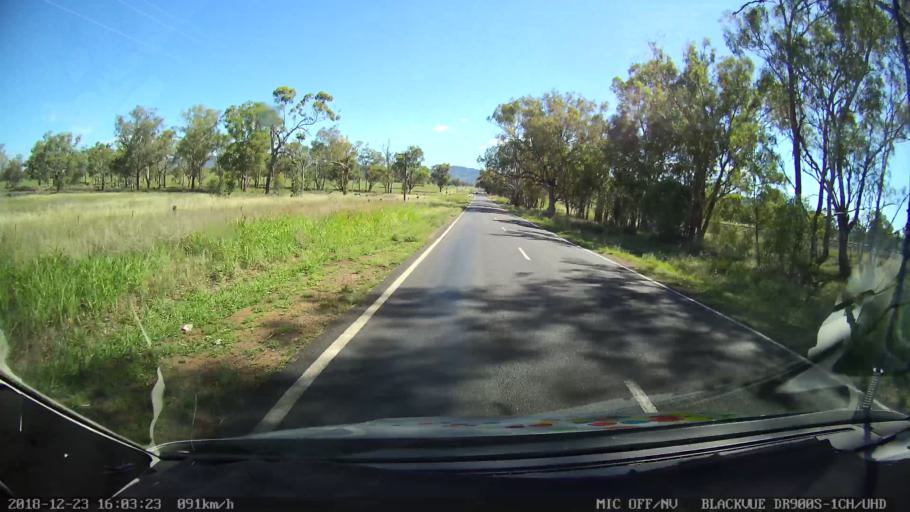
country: AU
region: New South Wales
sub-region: Tamworth Municipality
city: Phillip
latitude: -31.2429
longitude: 150.8011
